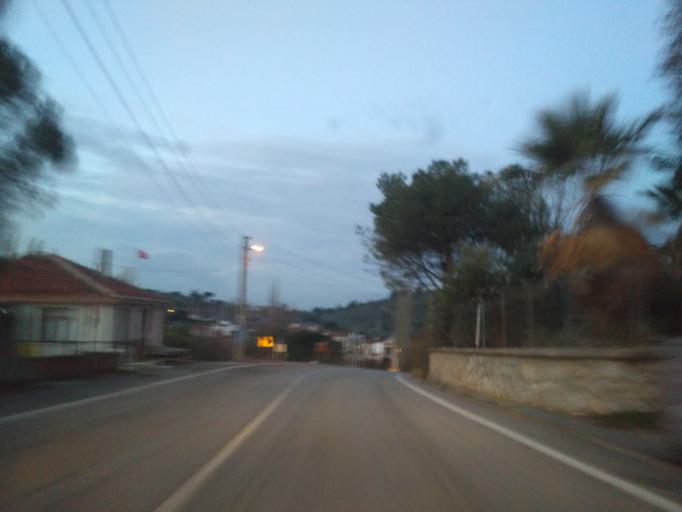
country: TR
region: Izmir
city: Buca
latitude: 38.3635
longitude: 27.2708
